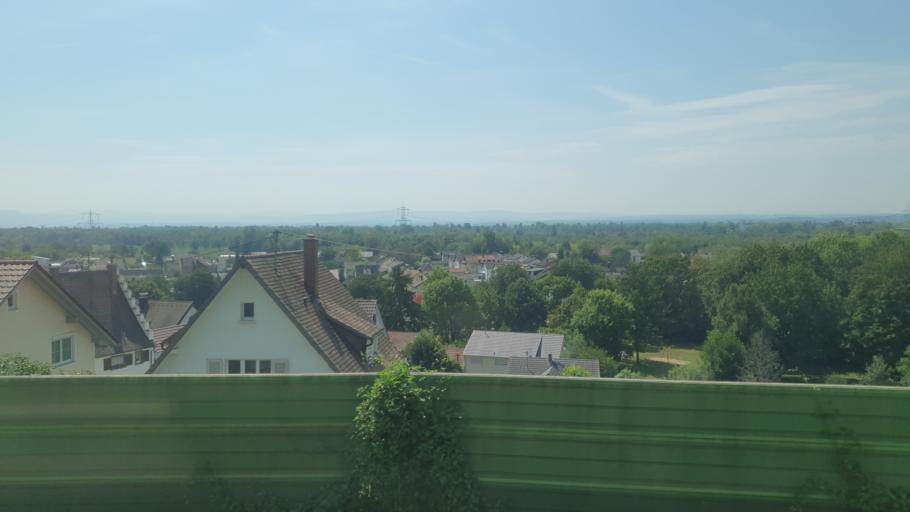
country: FR
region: Alsace
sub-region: Departement du Haut-Rhin
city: Rosenau
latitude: 47.6622
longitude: 7.5364
